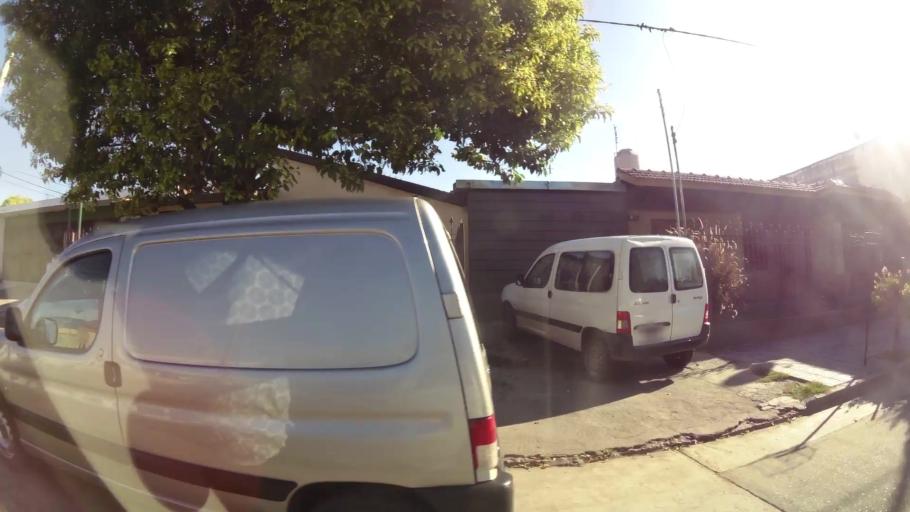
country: AR
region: Cordoba
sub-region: Departamento de Capital
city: Cordoba
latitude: -31.3849
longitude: -64.1676
